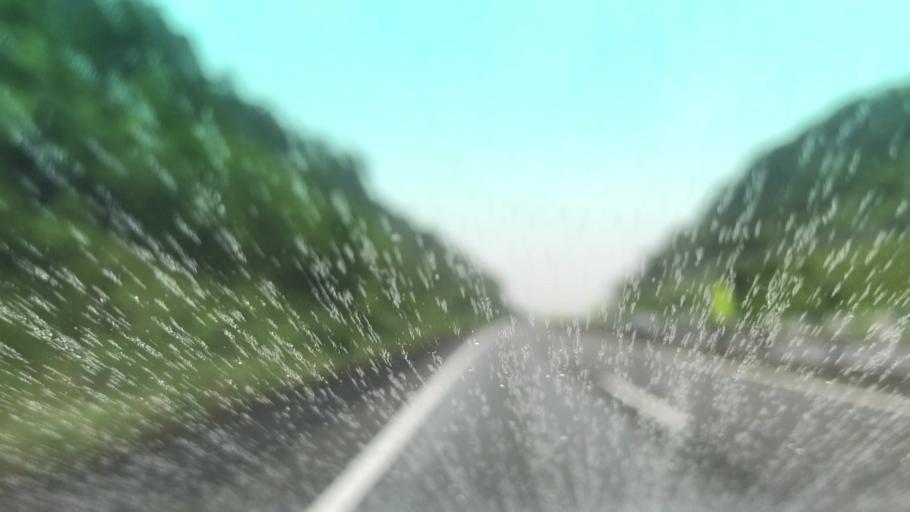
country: JP
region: Hokkaido
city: Shiraoi
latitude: 42.5562
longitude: 141.3141
